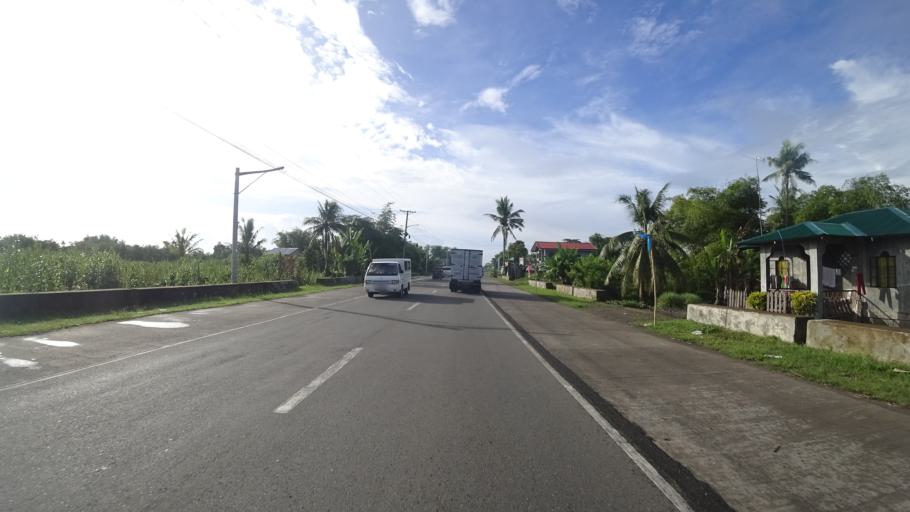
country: PH
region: Eastern Visayas
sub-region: Province of Leyte
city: Tanauan
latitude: 11.1271
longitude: 125.0104
